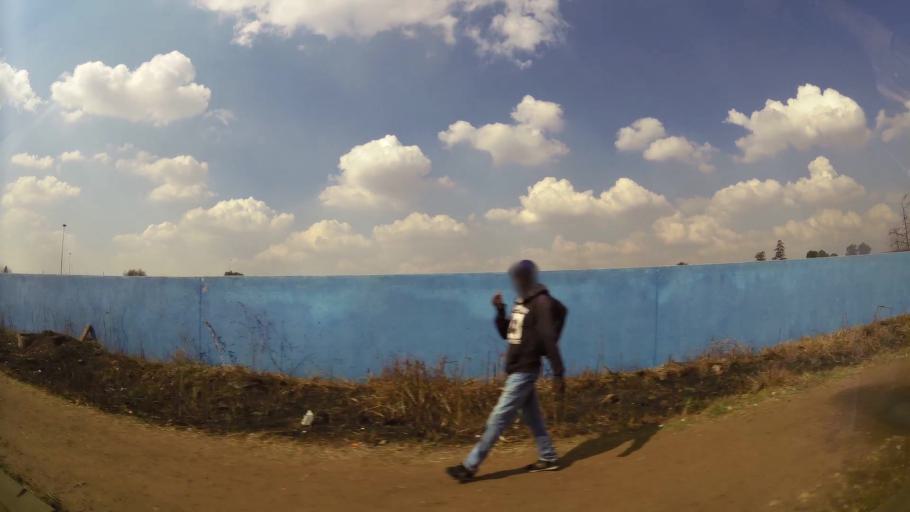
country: ZA
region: Gauteng
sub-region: Ekurhuleni Metropolitan Municipality
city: Germiston
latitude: -26.3220
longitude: 28.1427
